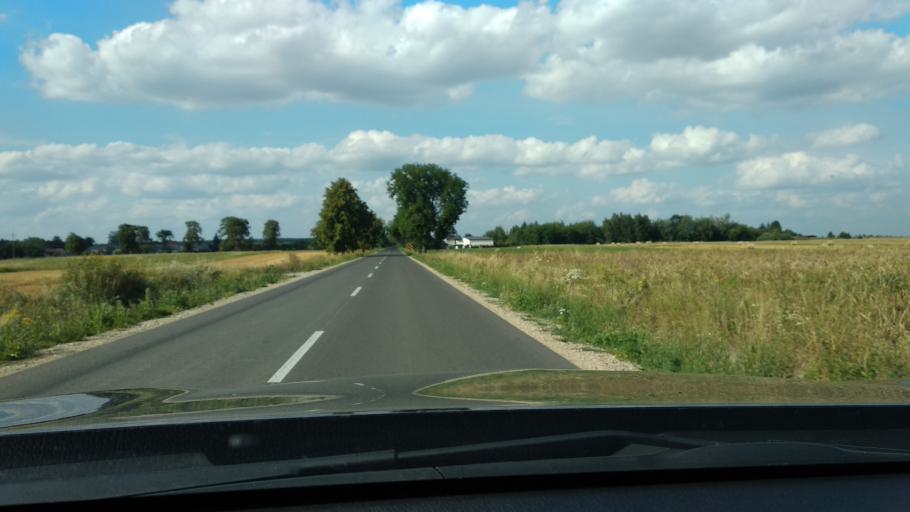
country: PL
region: Masovian Voivodeship
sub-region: Powiat pultuski
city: Zatory
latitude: 52.5562
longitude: 21.1876
